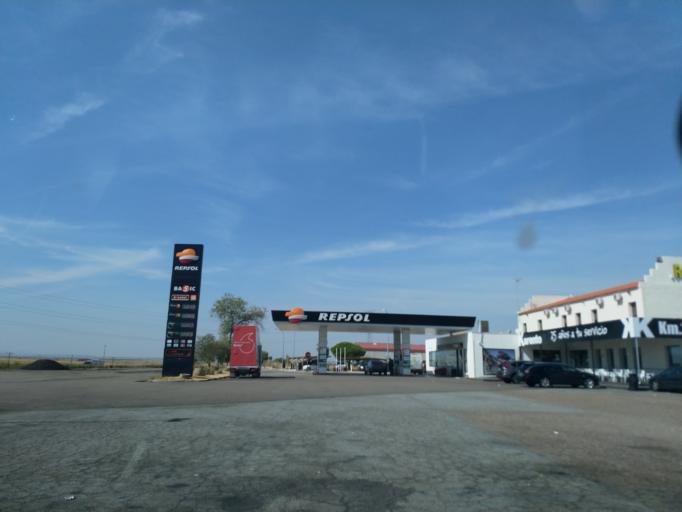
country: ES
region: Extremadura
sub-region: Provincia de Caceres
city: Berrocalejo
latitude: 39.8956
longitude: -5.3322
